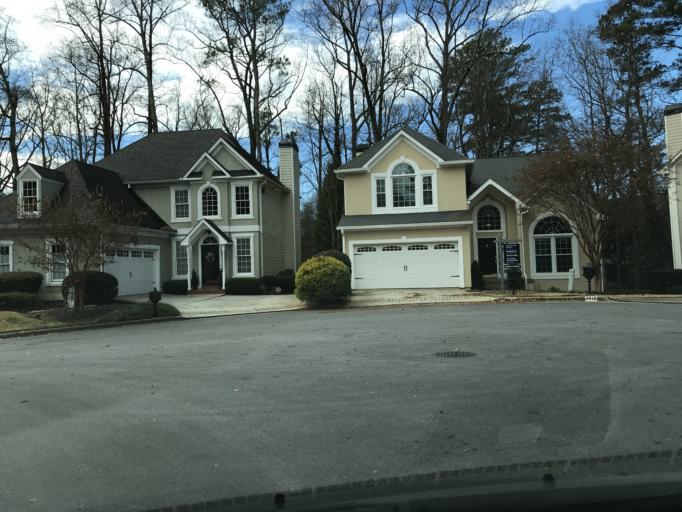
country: US
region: Georgia
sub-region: DeKalb County
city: North Atlanta
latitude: 33.8735
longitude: -84.3436
